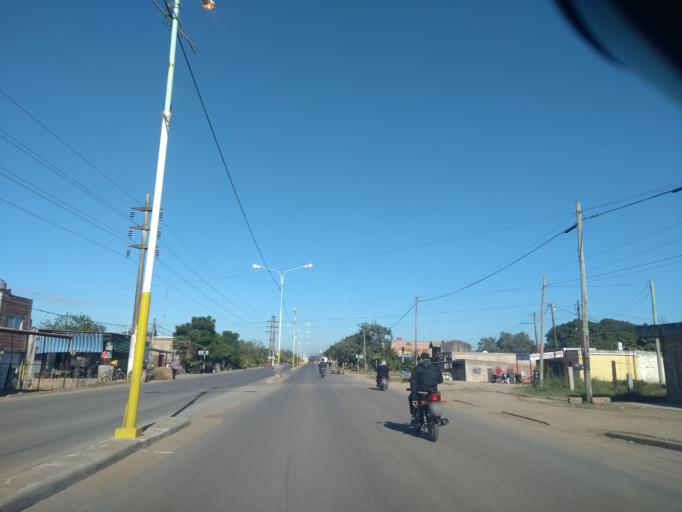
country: AR
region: Chaco
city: Barranqueras
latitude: -27.4737
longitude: -58.9260
